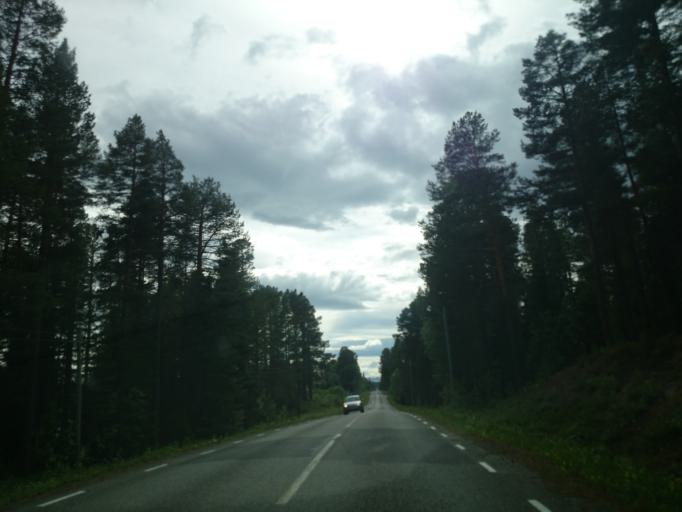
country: SE
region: Jaemtland
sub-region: Are Kommun
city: Are
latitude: 63.1854
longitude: 13.1256
